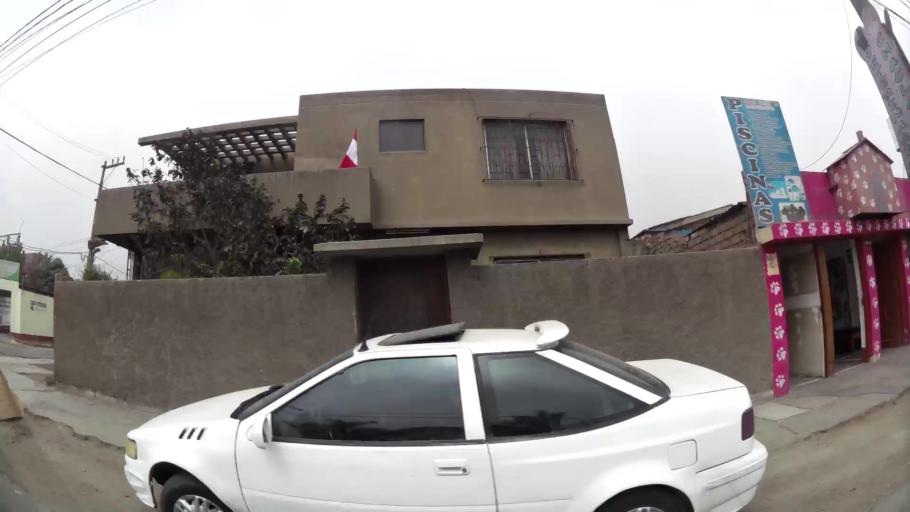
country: PE
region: Lima
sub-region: Lima
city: Chaclacayo
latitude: -11.9736
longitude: -76.7600
